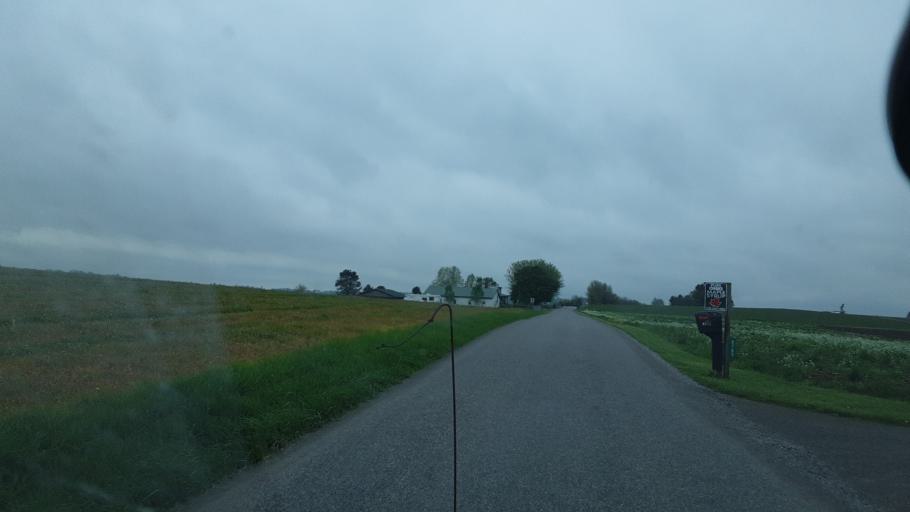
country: US
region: Ohio
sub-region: Holmes County
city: Millersburg
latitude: 40.5975
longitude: -81.8730
